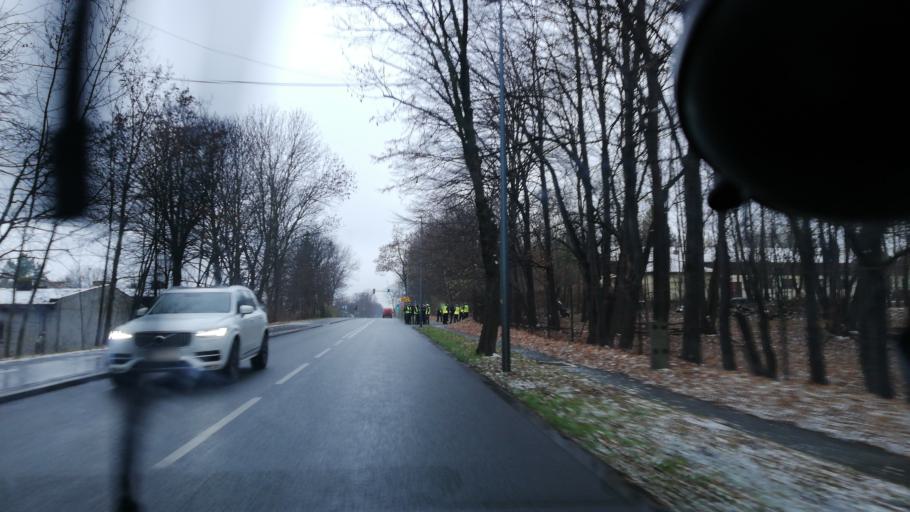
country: PL
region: Silesian Voivodeship
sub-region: Chorzow
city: Chorzow
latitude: 50.3005
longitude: 18.9833
